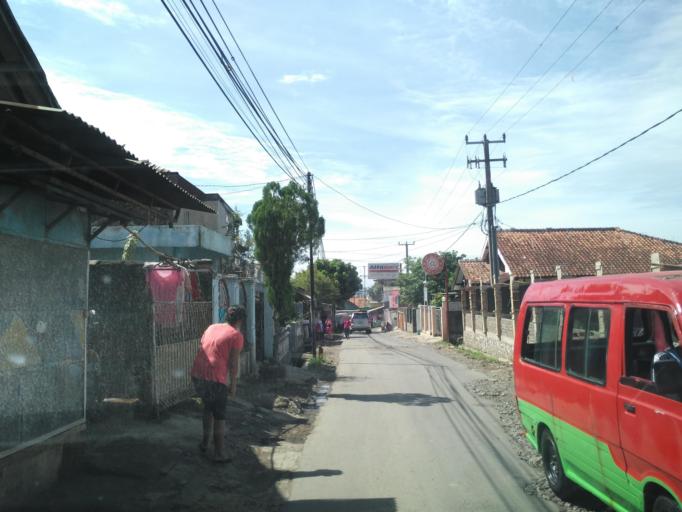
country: ID
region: West Java
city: Ciranjang-hilir
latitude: -6.8455
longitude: 107.1193
